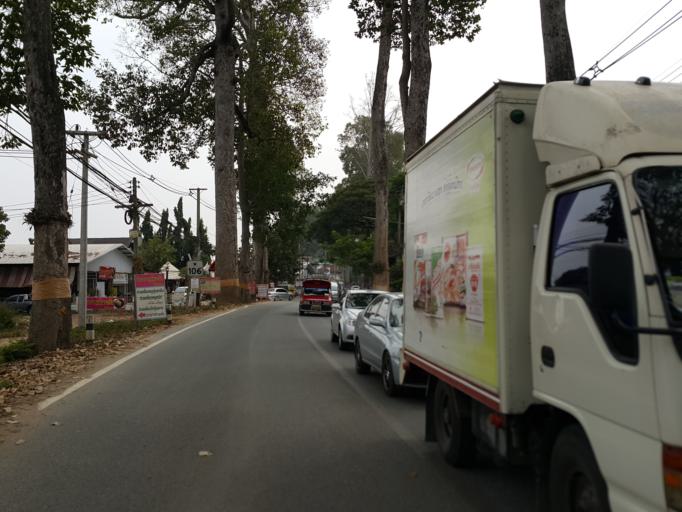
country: TH
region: Chiang Mai
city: Saraphi
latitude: 18.7288
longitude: 99.0236
